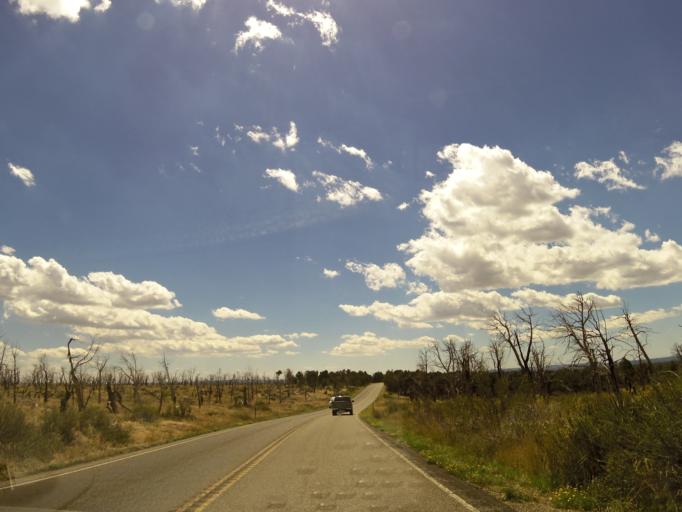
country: US
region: Colorado
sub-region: Montezuma County
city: Cortez
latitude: 37.1947
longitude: -108.4862
